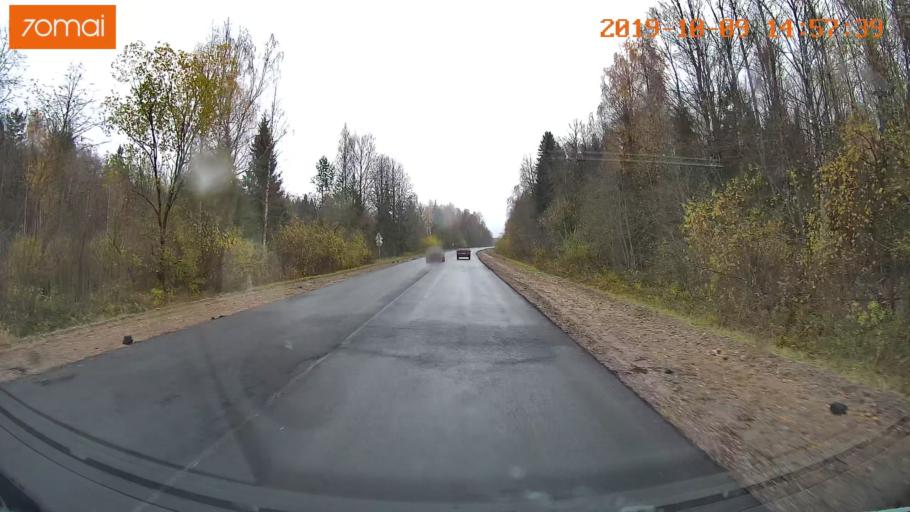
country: RU
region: Kostroma
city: Chistyye Bory
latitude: 58.3355
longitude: 41.6518
